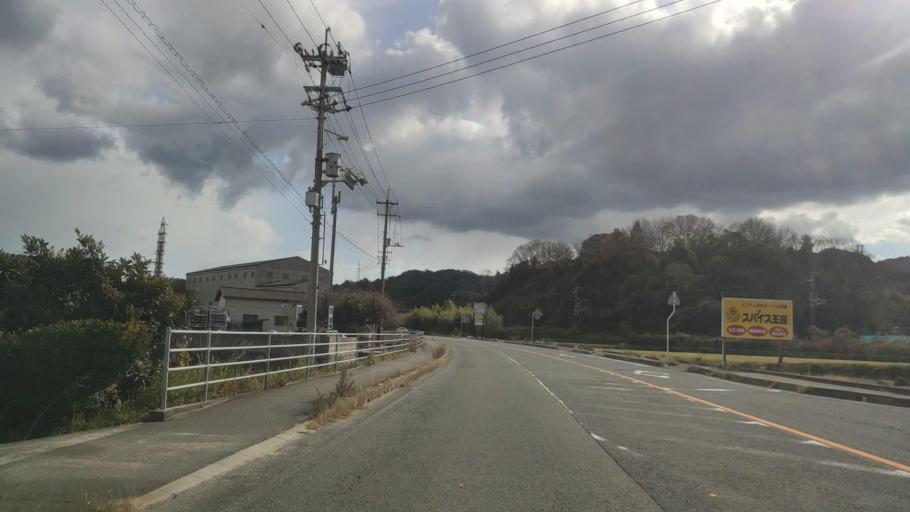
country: JP
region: Ehime
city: Hojo
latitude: 34.0578
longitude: 132.8853
